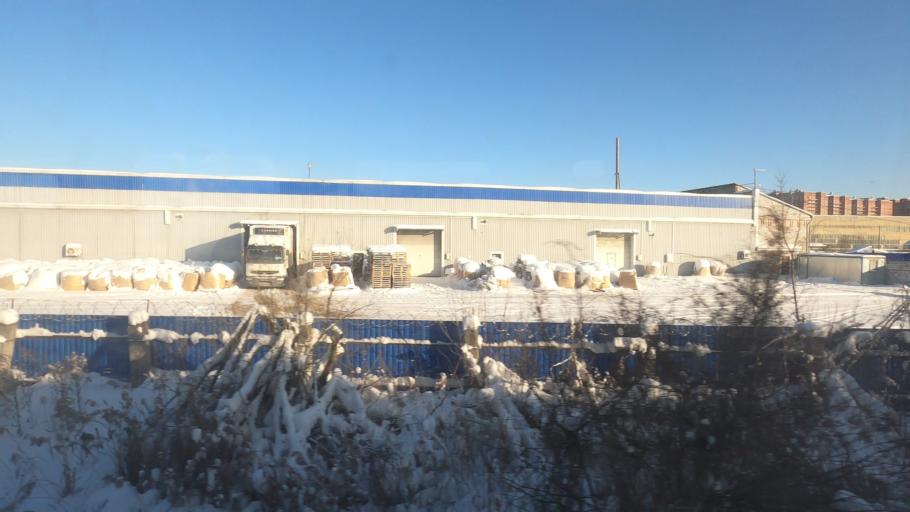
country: RU
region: Moskovskaya
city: Dmitrov
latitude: 56.3762
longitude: 37.5217
